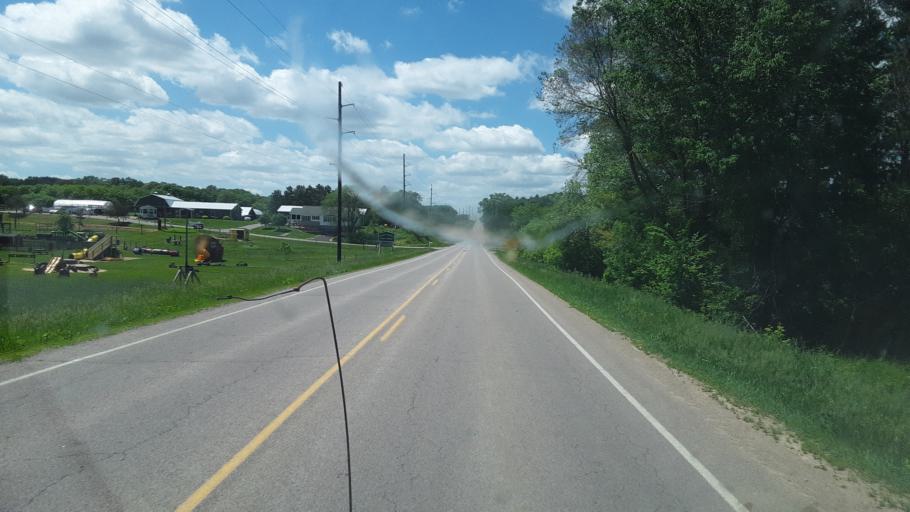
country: US
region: Wisconsin
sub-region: Sauk County
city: Lake Delton
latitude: 43.5906
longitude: -89.8333
